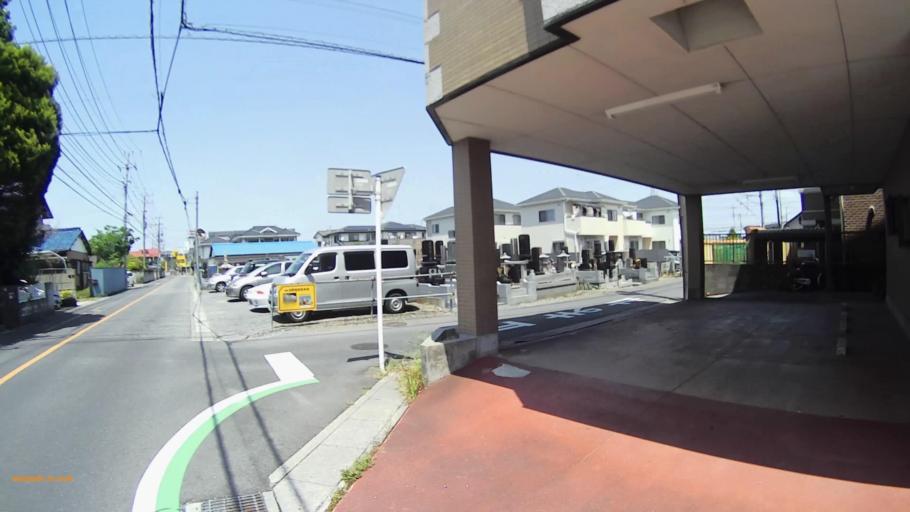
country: JP
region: Saitama
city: Koshigaya
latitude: 35.9203
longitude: 139.7820
